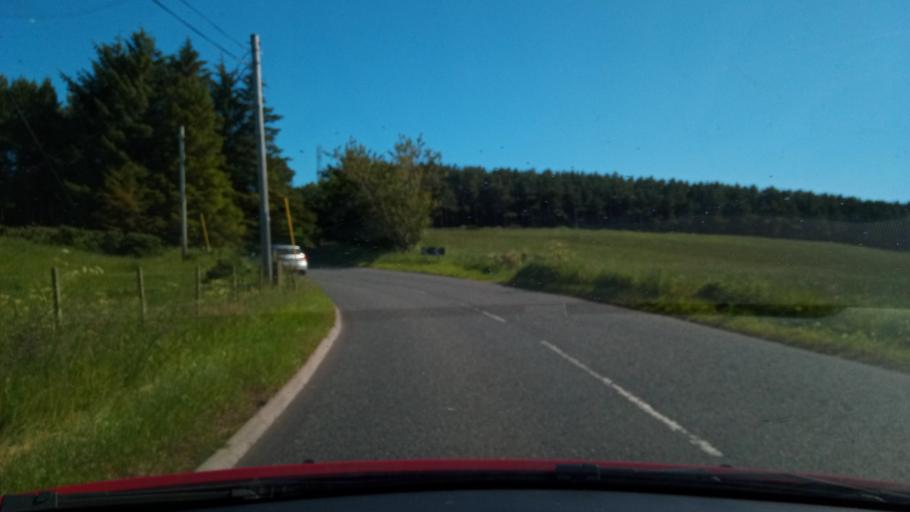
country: GB
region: Scotland
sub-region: The Scottish Borders
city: Duns
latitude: 55.8285
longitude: -2.3296
